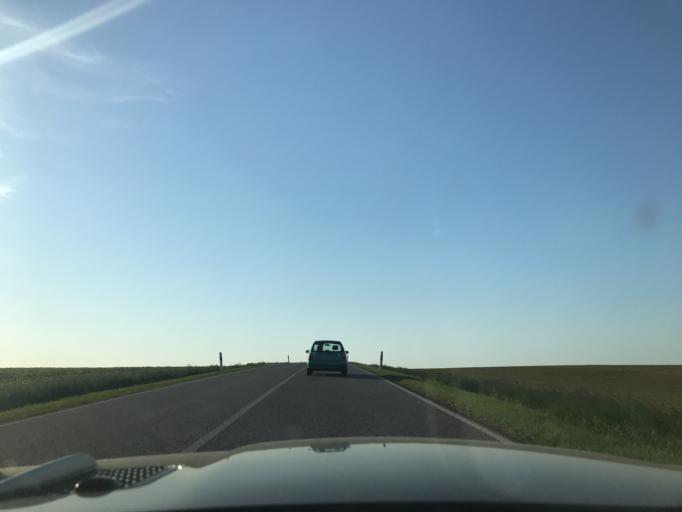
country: DE
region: Thuringia
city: Bad Langensalza
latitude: 51.0616
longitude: 10.6473
